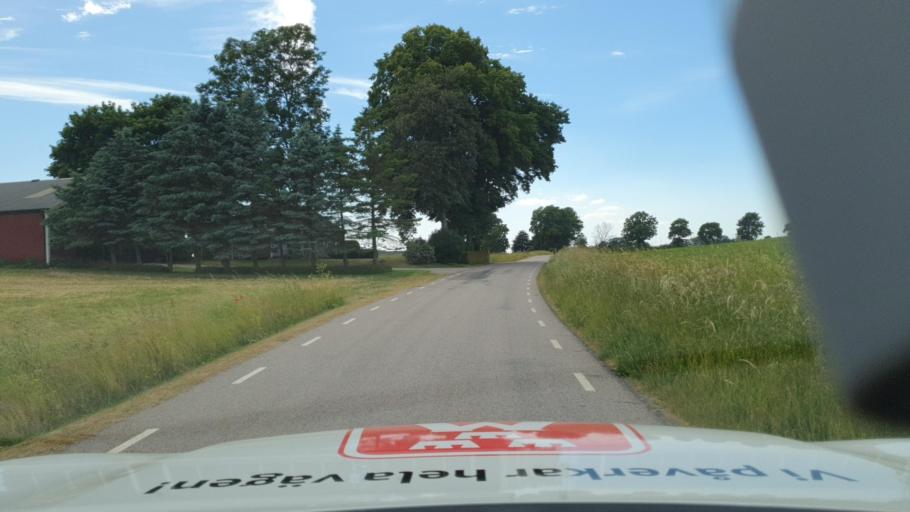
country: SE
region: Skane
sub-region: Tomelilla Kommun
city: Tomelilla
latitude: 55.6283
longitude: 13.8458
